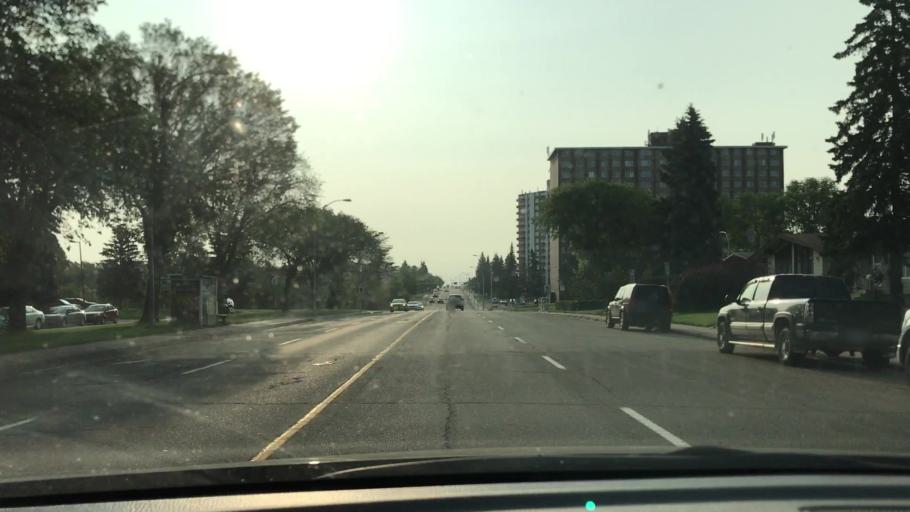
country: CA
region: Alberta
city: Edmonton
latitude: 53.5409
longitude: -113.4340
